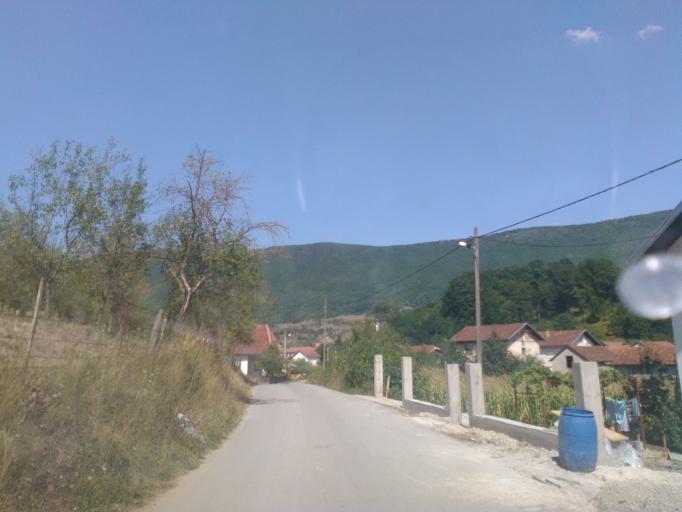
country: BA
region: Federation of Bosnia and Herzegovina
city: Orasac
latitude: 44.6244
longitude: 16.0660
